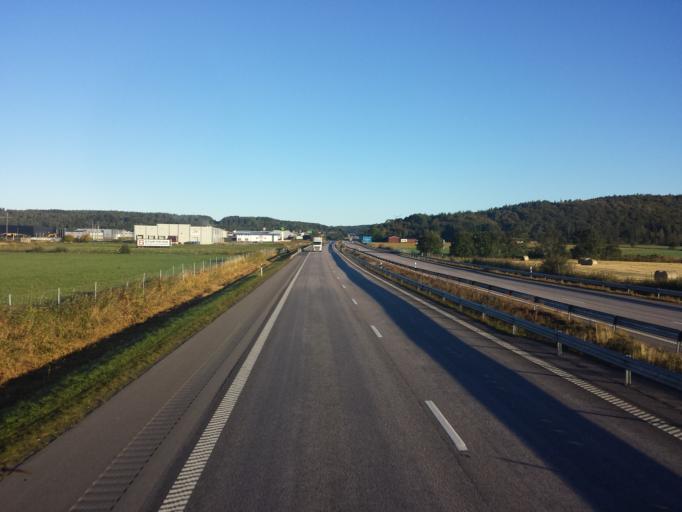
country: SE
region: Halland
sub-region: Varbergs Kommun
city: Varberg
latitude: 57.1585
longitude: 12.2877
